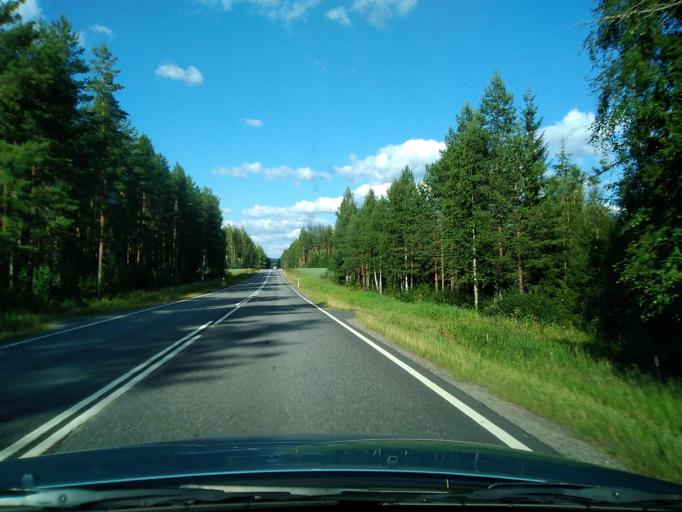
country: FI
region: Pirkanmaa
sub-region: Ylae-Pirkanmaa
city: Maenttae
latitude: 61.9636
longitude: 24.5926
